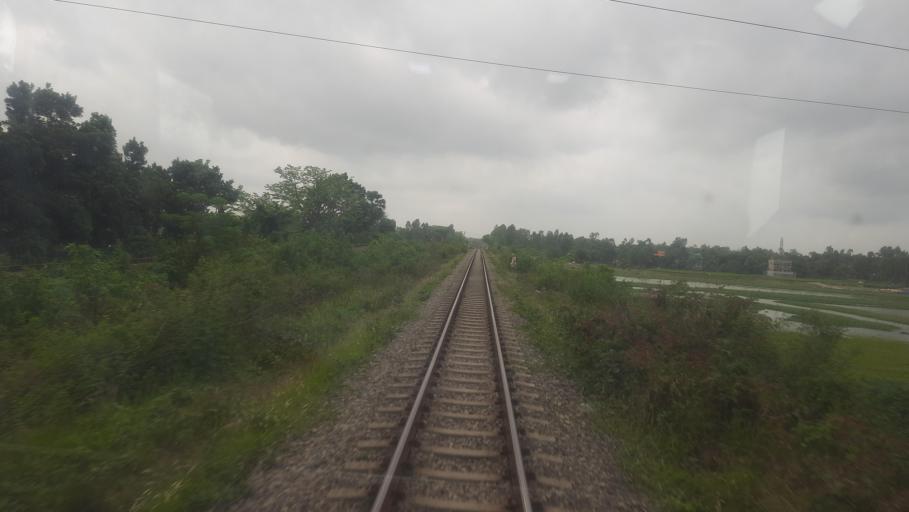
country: BD
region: Dhaka
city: Bhairab Bazar
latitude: 24.0393
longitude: 90.9633
